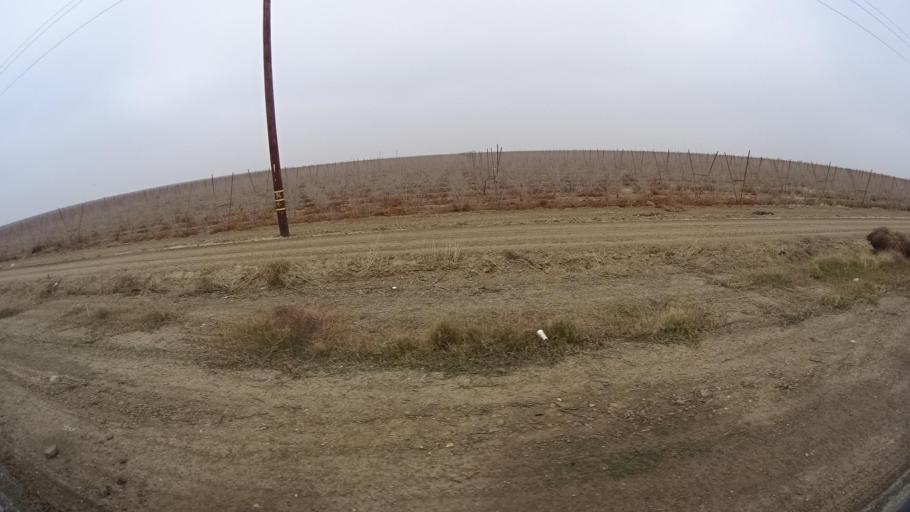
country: US
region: California
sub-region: Kern County
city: Maricopa
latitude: 35.0937
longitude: -119.2456
